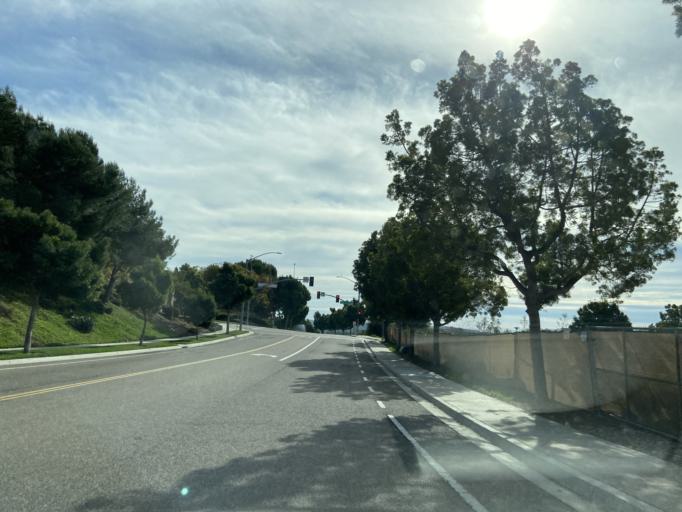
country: US
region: California
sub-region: San Diego County
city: Lake San Marcos
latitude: 33.1264
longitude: -117.2618
